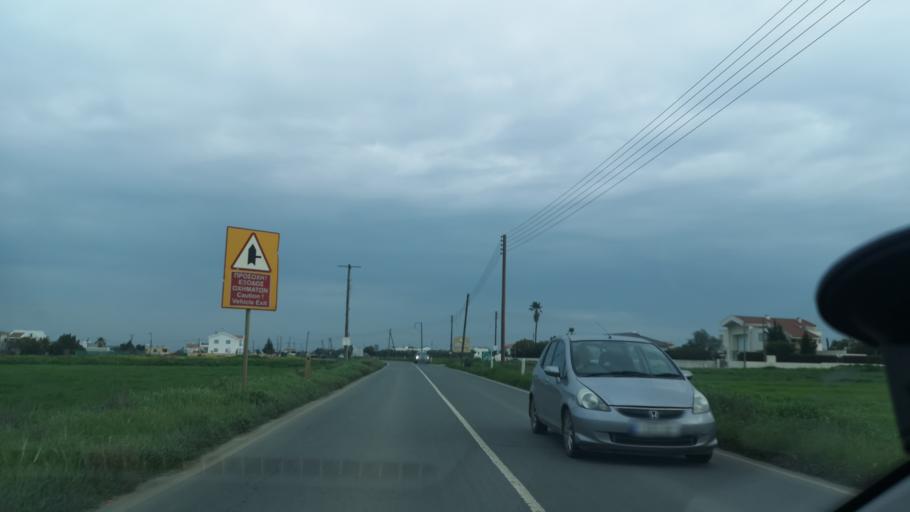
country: CY
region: Lefkosia
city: Tseri
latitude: 35.0784
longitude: 33.3083
